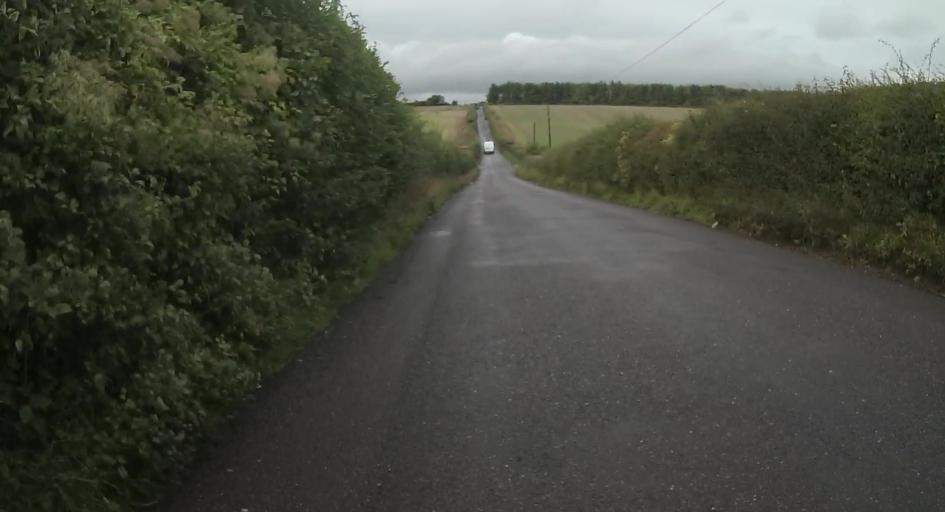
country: GB
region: England
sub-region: Hampshire
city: Tadley
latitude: 51.2903
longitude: -1.1462
